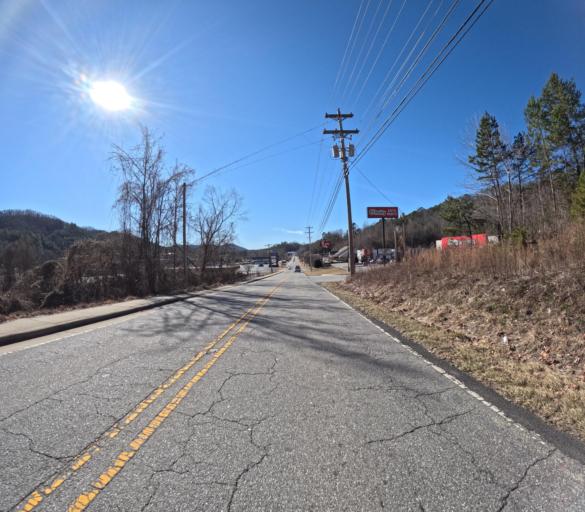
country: US
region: North Carolina
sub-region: Cherokee County
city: Murphy
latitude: 35.1060
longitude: -84.0131
